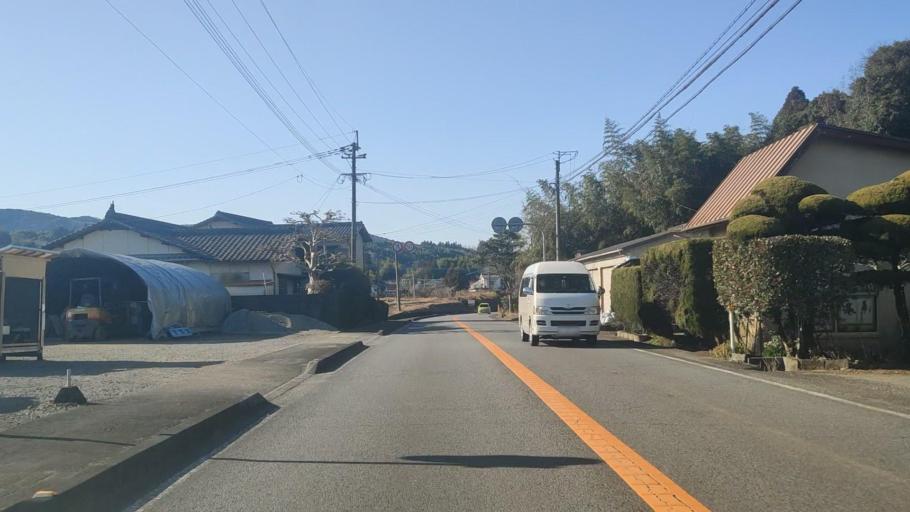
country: JP
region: Oita
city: Usuki
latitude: 33.0556
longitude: 131.6804
